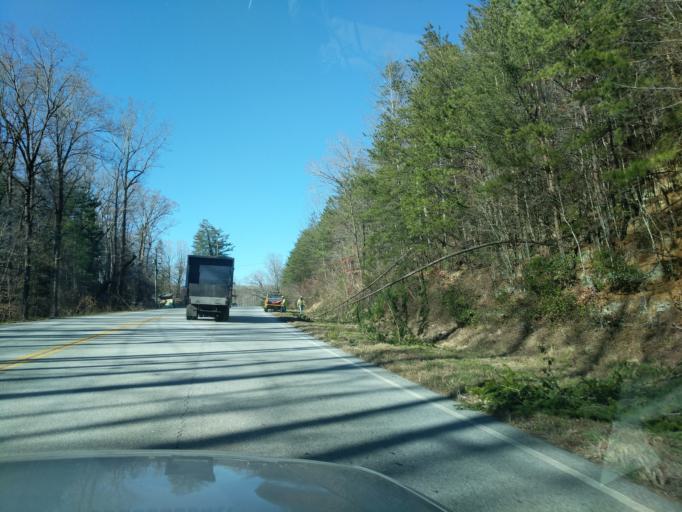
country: US
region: Georgia
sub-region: Rabun County
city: Clayton
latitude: 34.8608
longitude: -83.3888
